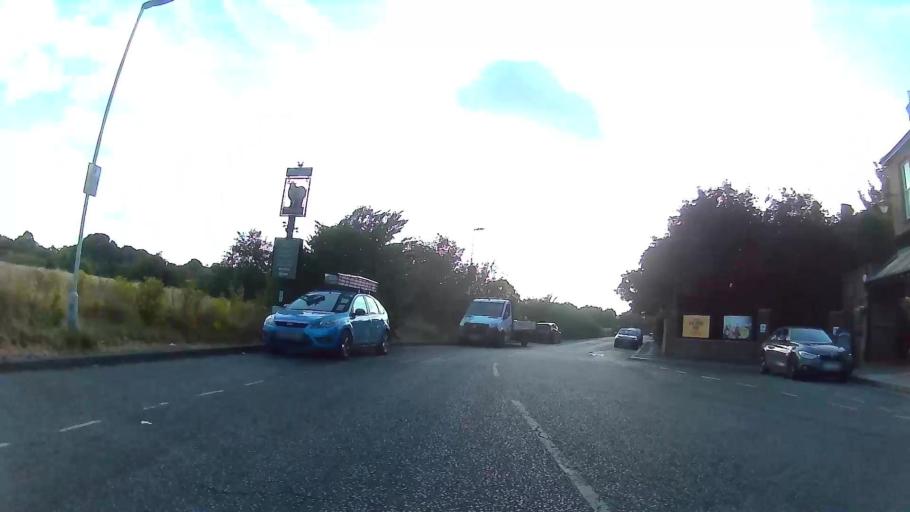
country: GB
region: England
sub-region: Greater London
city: East Ham
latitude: 51.5550
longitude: 0.0420
